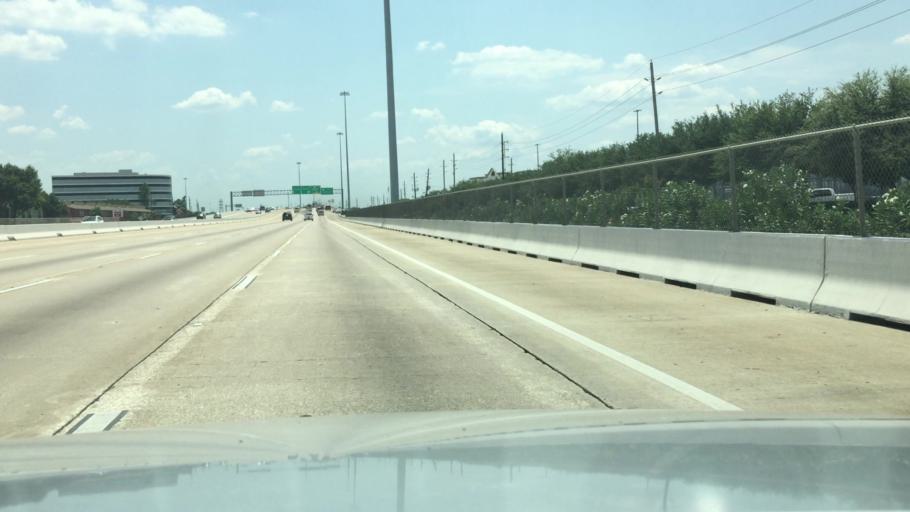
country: US
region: Texas
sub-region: Fort Bend County
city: Meadows Place
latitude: 29.6800
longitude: -95.5595
